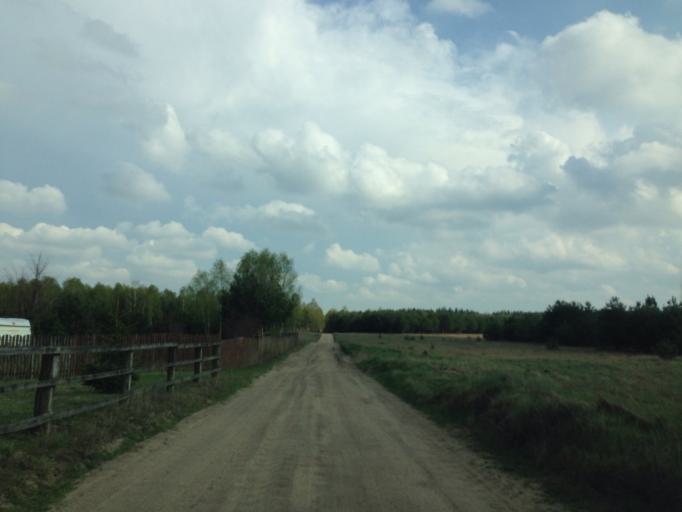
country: PL
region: Kujawsko-Pomorskie
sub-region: Powiat brodnicki
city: Gorzno
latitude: 53.1532
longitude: 19.6524
